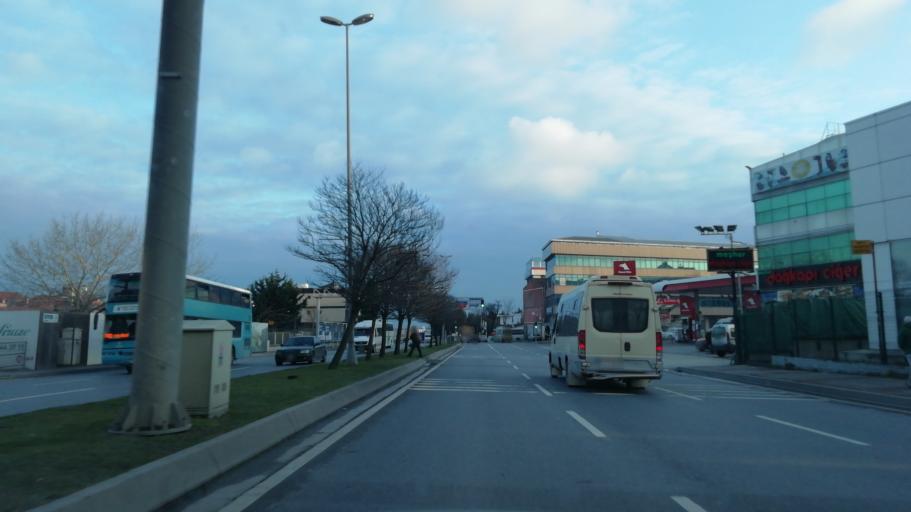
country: TR
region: Istanbul
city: Yakuplu
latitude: 40.9915
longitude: 28.7184
